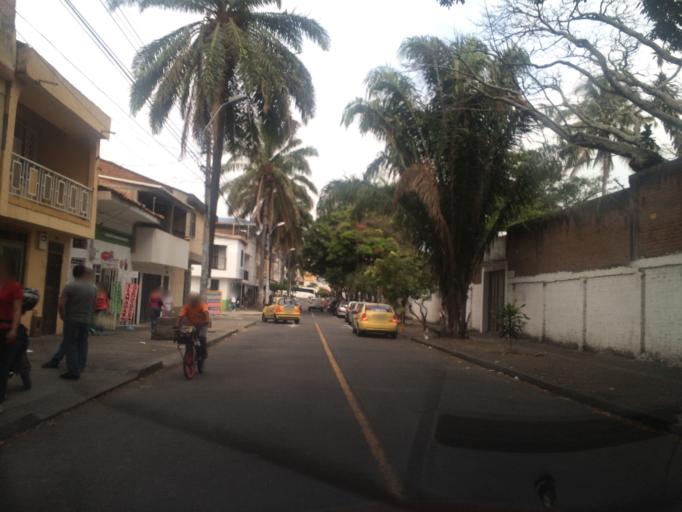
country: CO
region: Valle del Cauca
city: Cali
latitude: 3.4408
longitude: -76.5385
